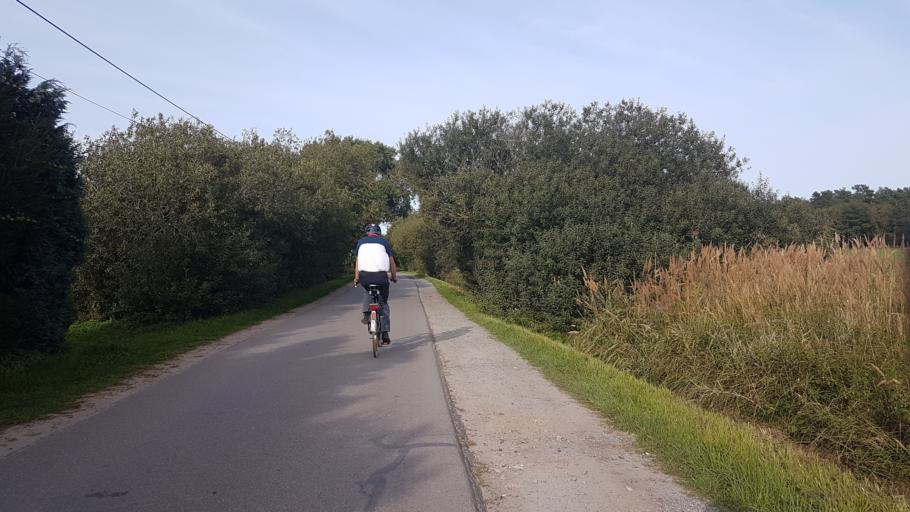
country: DE
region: Mecklenburg-Vorpommern
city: Hiddensee
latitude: 54.4632
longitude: 13.1381
